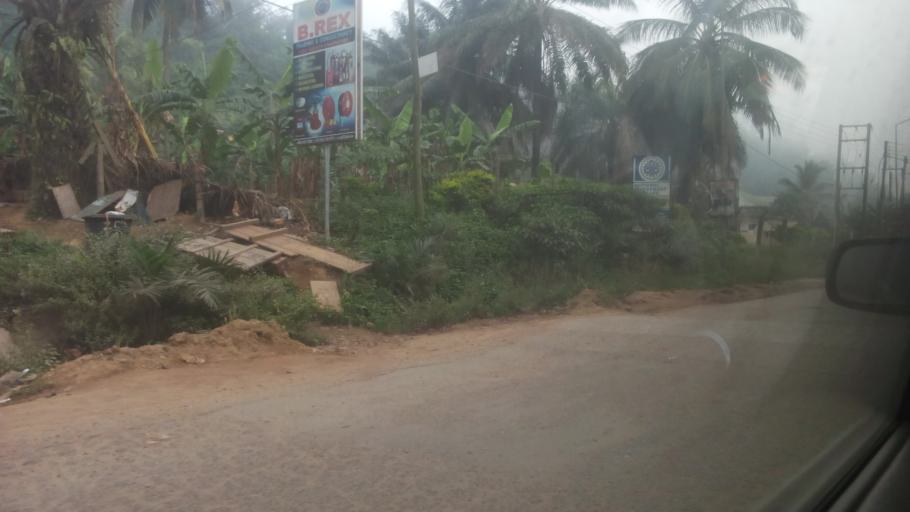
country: GH
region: Western
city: Tarkwa
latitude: 5.2776
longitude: -2.0039
